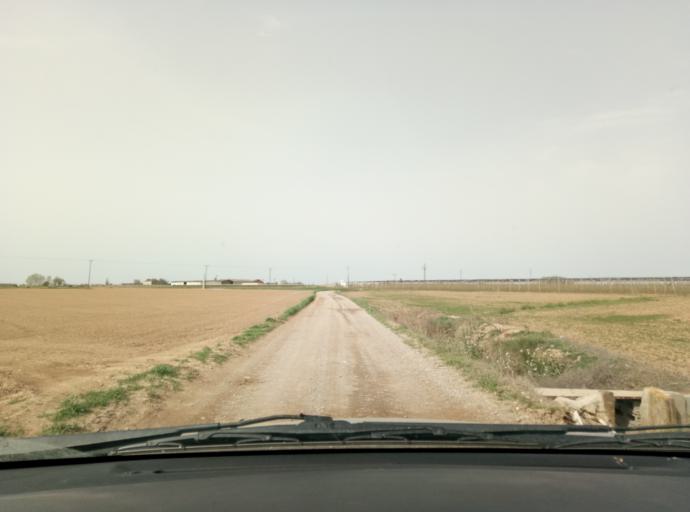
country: ES
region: Catalonia
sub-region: Provincia de Lleida
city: La Fuliola
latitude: 41.7142
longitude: 1.0361
